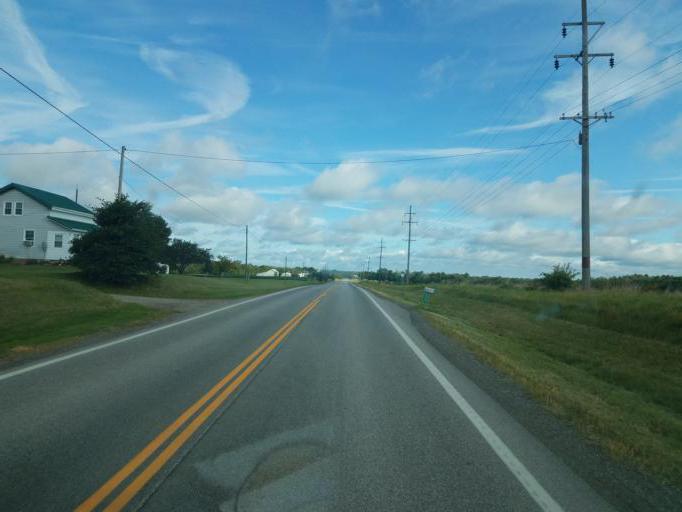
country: US
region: Ohio
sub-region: Wayne County
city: West Salem
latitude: 41.0472
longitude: -82.1258
